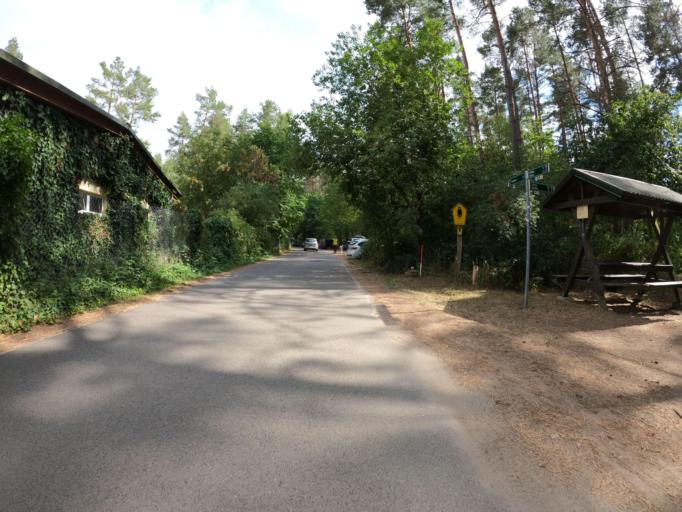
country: DE
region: Brandenburg
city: Lychen
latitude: 53.2829
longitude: 13.4295
